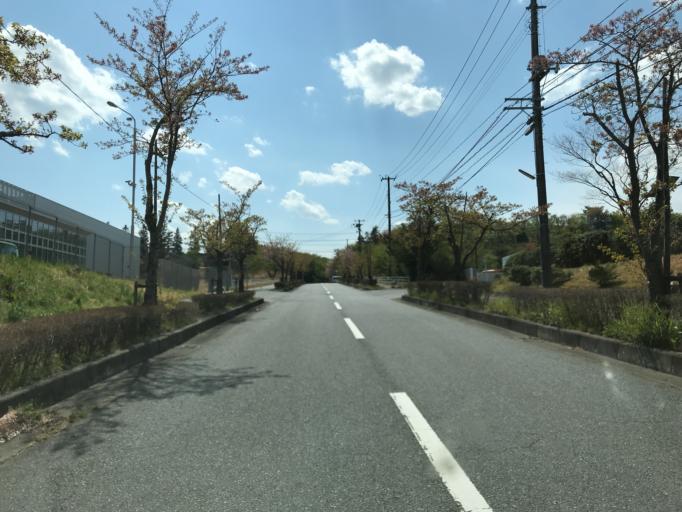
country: JP
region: Fukushima
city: Iwaki
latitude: 37.0761
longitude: 140.8533
